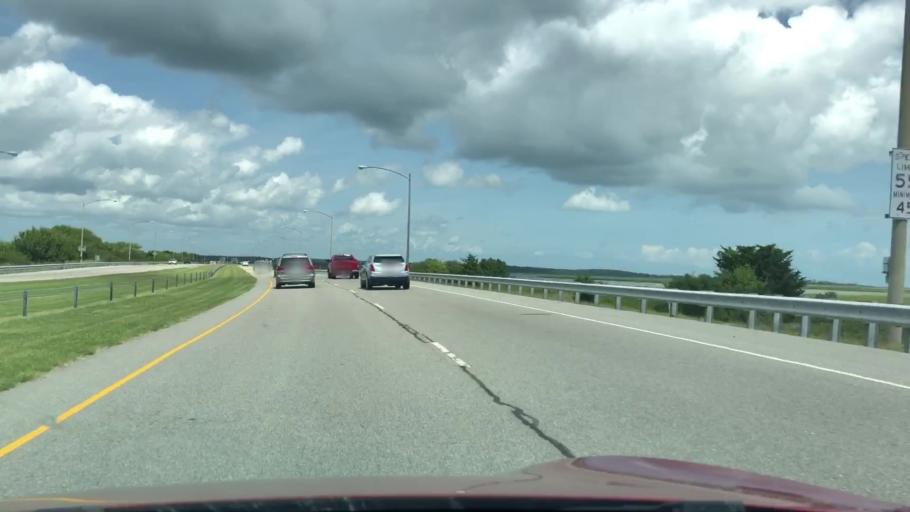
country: US
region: Virginia
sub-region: Northampton County
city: Cape Charles
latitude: 37.0980
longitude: -75.9691
